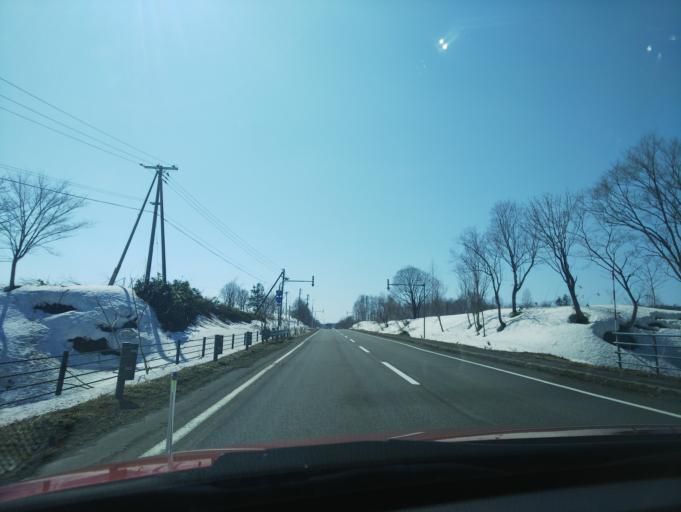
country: JP
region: Hokkaido
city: Nayoro
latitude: 44.6805
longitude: 142.2681
